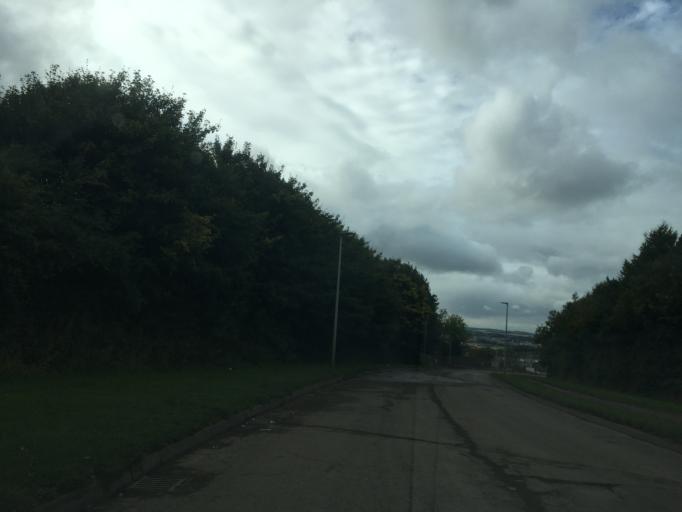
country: GB
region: Scotland
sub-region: Midlothian
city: Gorebridge
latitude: 55.8650
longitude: -3.0517
